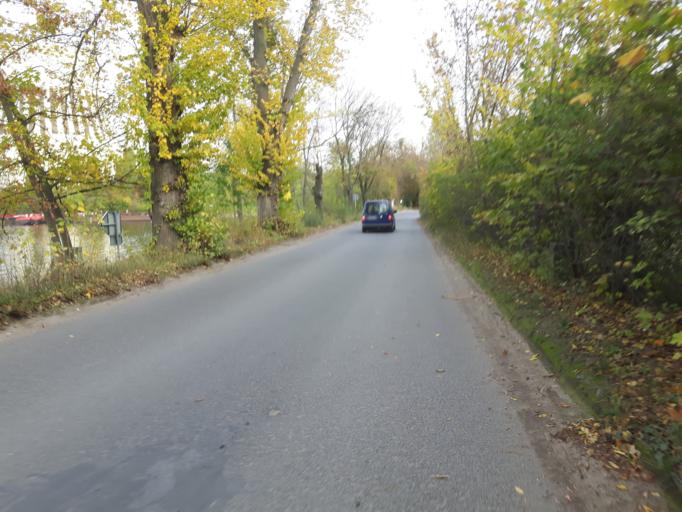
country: DE
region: Berlin
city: Haselhorst
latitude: 52.5336
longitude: 13.2332
